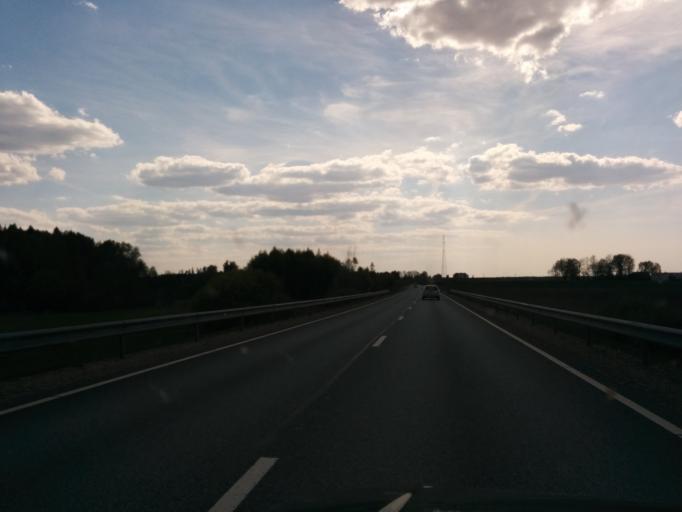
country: LV
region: Sigulda
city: Sigulda
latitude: 57.2260
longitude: 24.8008
